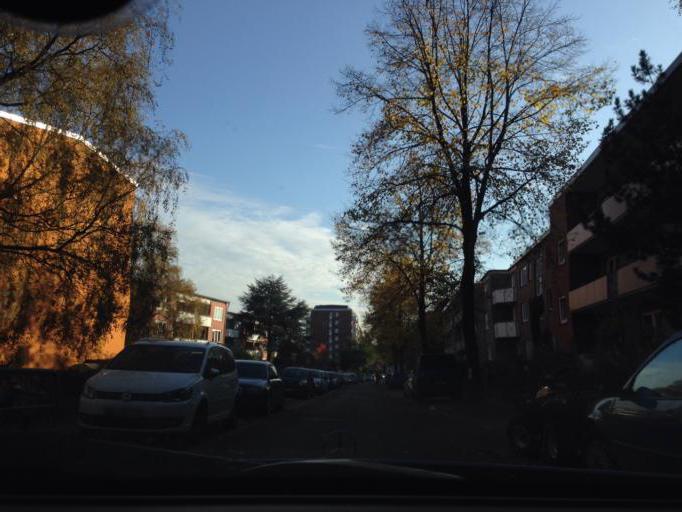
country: DE
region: Hamburg
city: Marienthal
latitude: 53.5827
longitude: 10.0824
